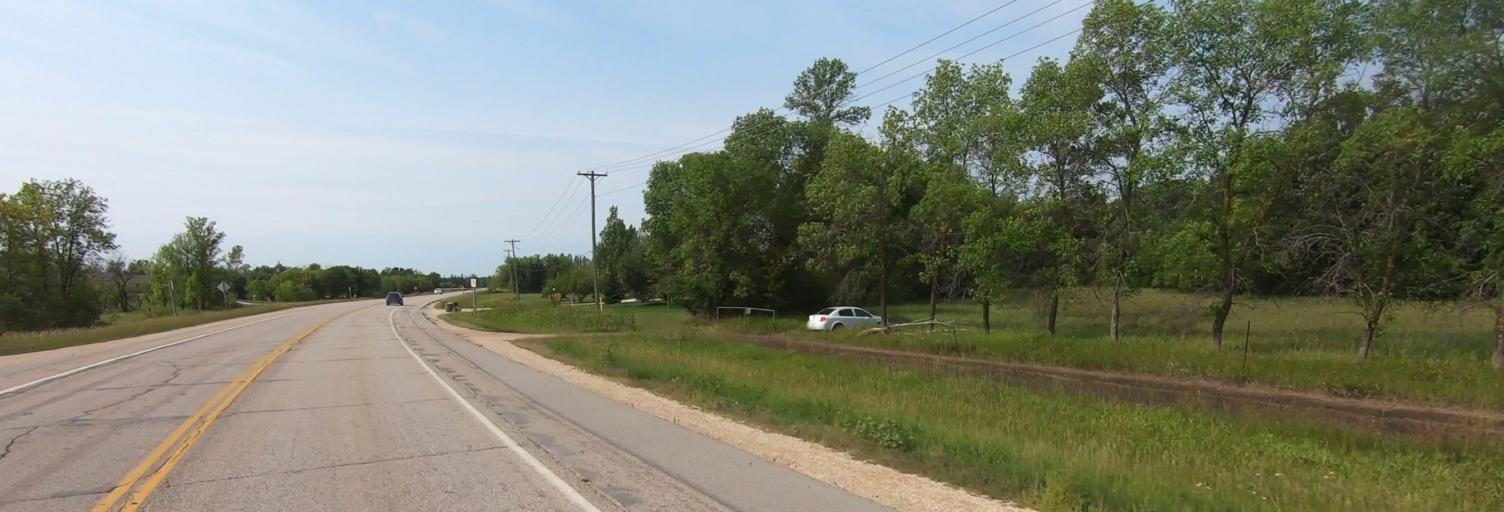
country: CA
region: Manitoba
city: Niverville
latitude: 49.6957
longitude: -97.0992
